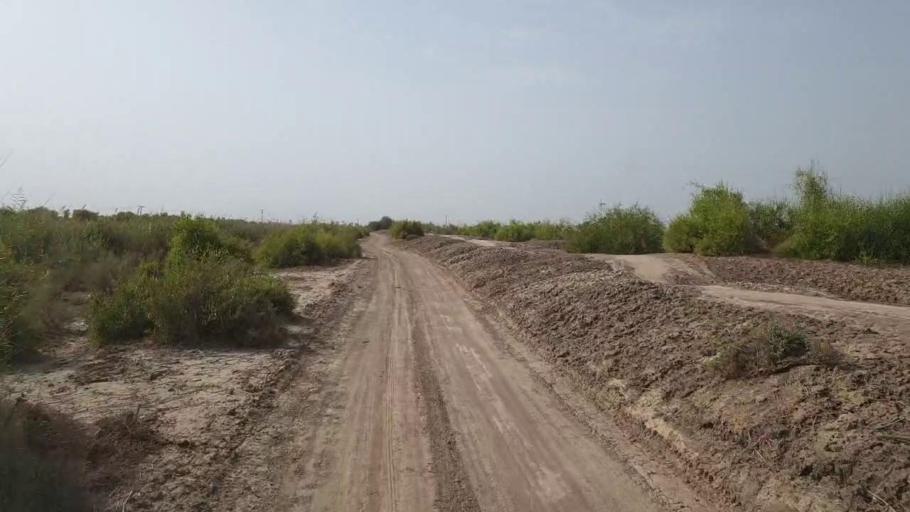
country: PK
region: Sindh
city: Daur
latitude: 26.4287
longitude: 68.1579
